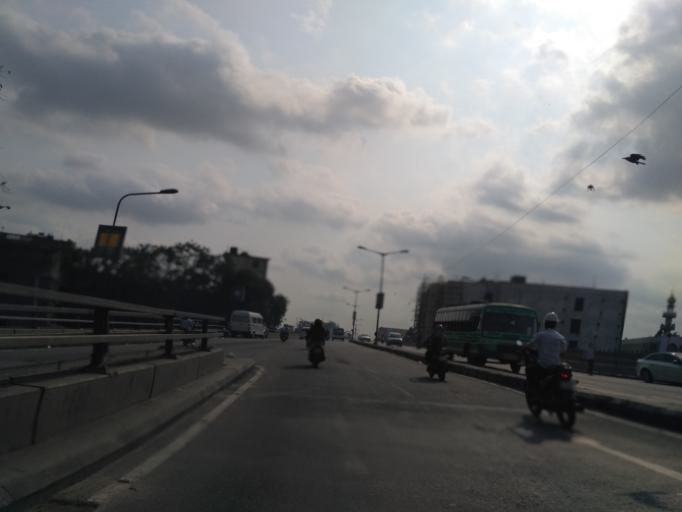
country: IN
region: Karnataka
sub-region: Bangalore Urban
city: Bangalore
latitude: 12.9647
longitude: 77.5750
